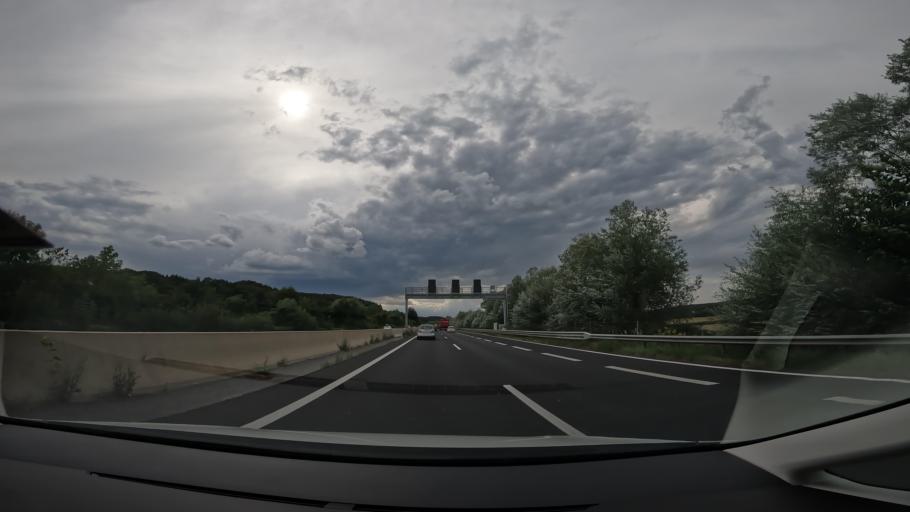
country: AT
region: Styria
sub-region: Politischer Bezirk Hartberg-Fuerstenfeld
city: Nestelbach im Ilztal
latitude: 47.0889
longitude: 15.8582
